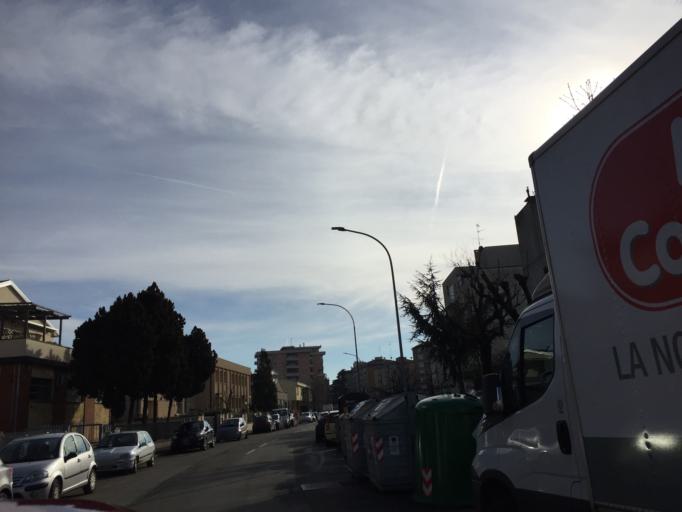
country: IT
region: Emilia-Romagna
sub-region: Provincia di Bologna
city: Bologna
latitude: 44.5033
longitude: 11.3046
